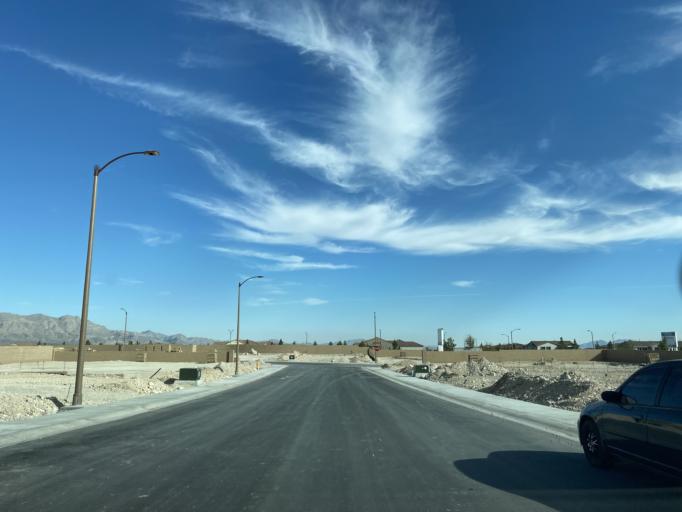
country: US
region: Nevada
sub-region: Clark County
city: Summerlin South
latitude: 36.3109
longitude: -115.3167
